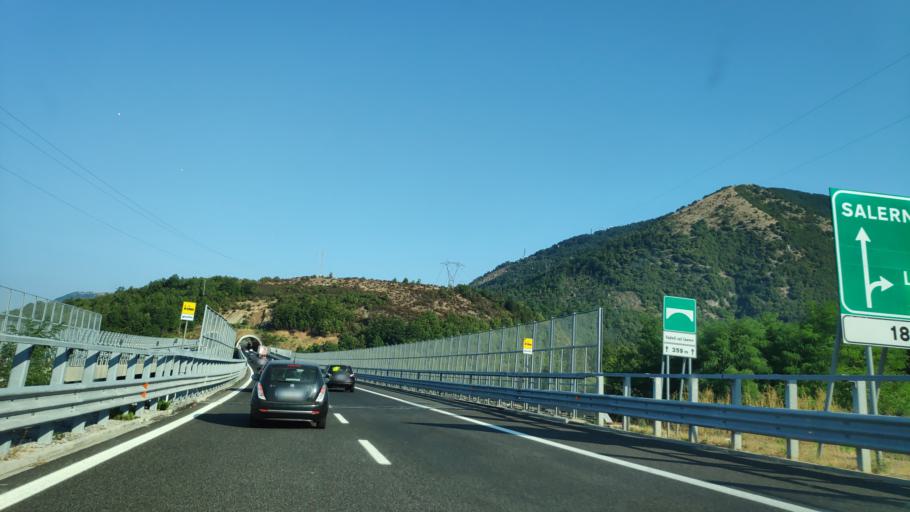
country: IT
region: Basilicate
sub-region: Provincia di Potenza
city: Lagonegro
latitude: 40.1233
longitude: 15.7822
